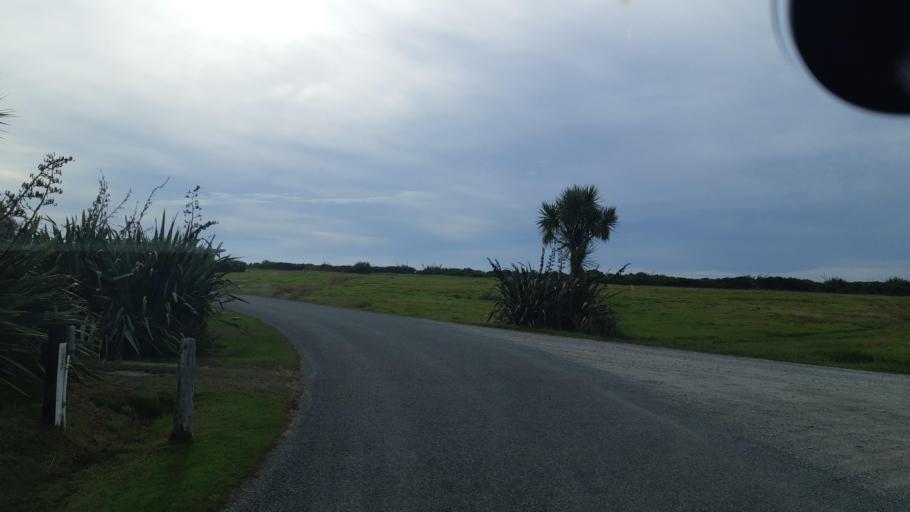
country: NZ
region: West Coast
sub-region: Westland District
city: Hokitika
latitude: -43.2218
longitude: 170.1672
